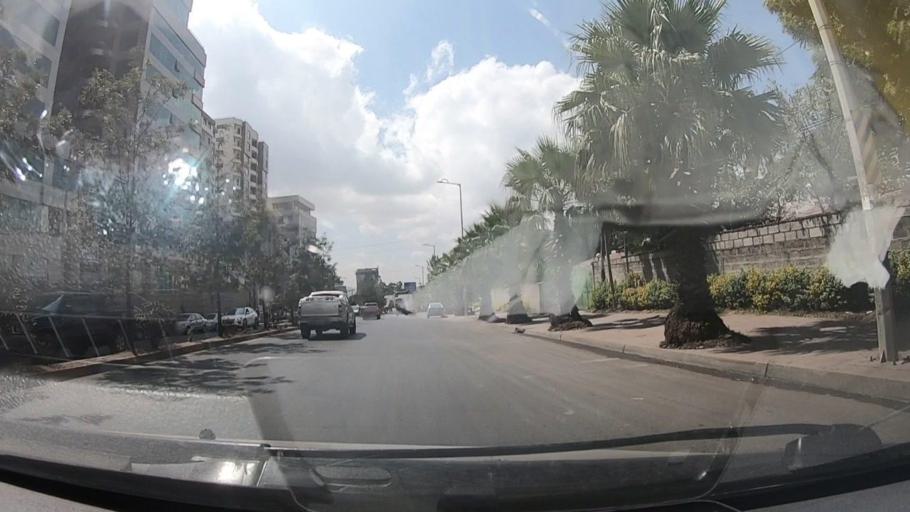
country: ET
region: Adis Abeba
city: Addis Ababa
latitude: 8.9901
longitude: 38.7245
